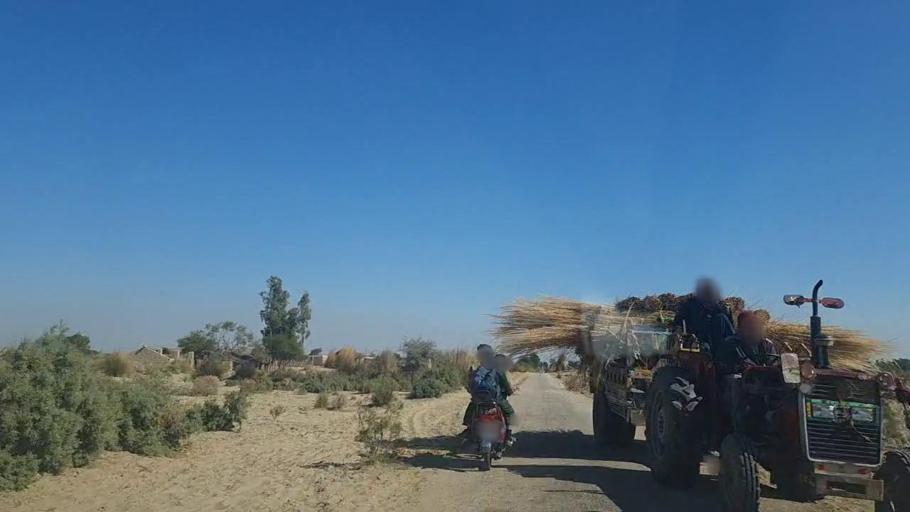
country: PK
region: Sindh
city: Khadro
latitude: 26.2094
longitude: 68.8408
